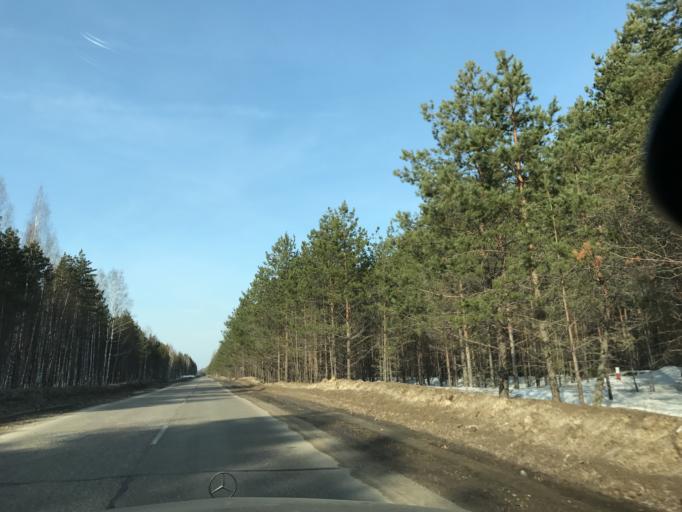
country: RU
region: Vladimir
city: Galitsy
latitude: 56.0478
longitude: 42.8639
